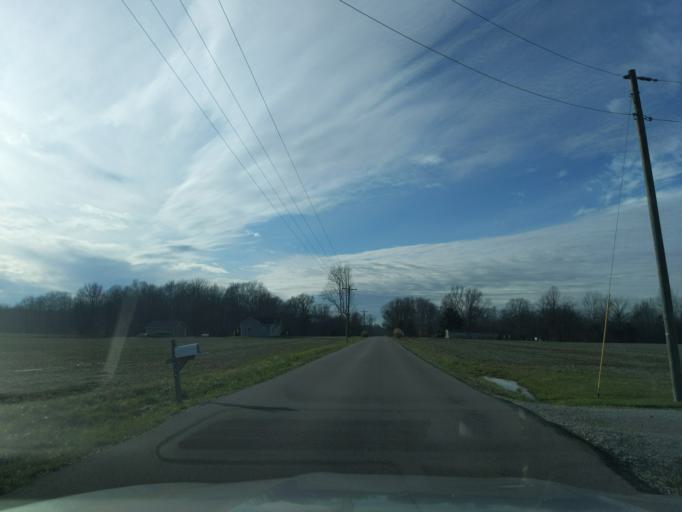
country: US
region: Indiana
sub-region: Decatur County
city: Westport
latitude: 39.1903
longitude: -85.5031
